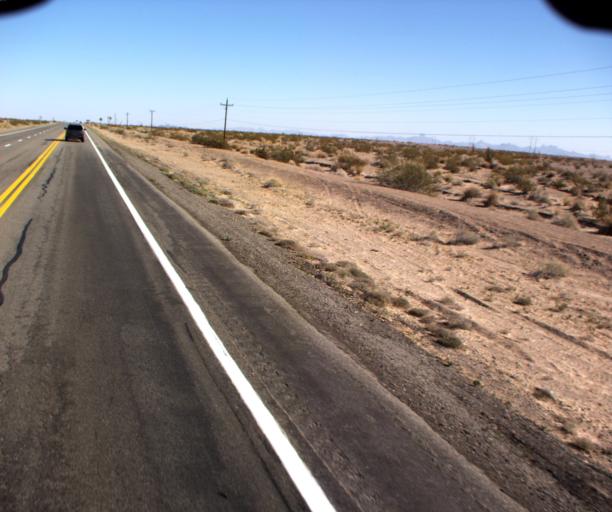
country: US
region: Arizona
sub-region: Yuma County
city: Fortuna Foothills
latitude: 32.8127
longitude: -114.3795
